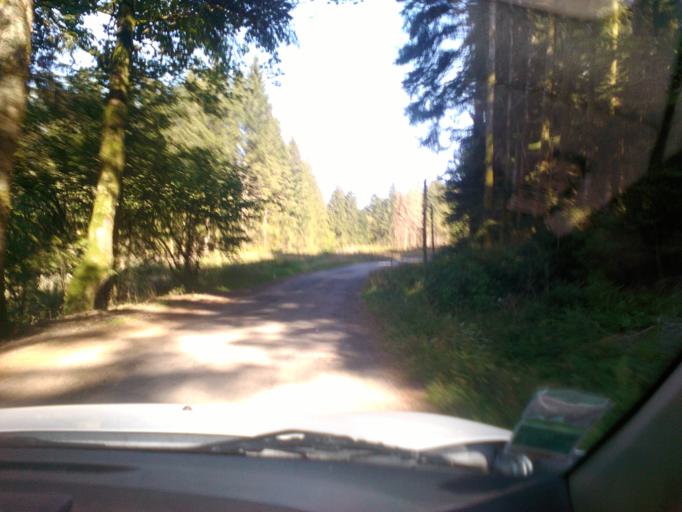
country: FR
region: Lorraine
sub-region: Departement des Vosges
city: Le Tholy
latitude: 48.0647
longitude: 6.7867
